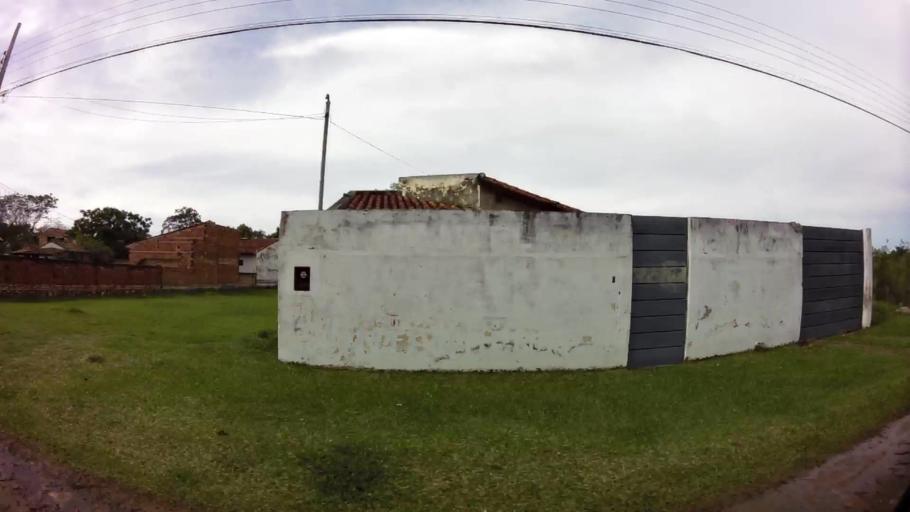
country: PY
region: Central
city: Limpio
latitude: -25.1650
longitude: -57.4799
